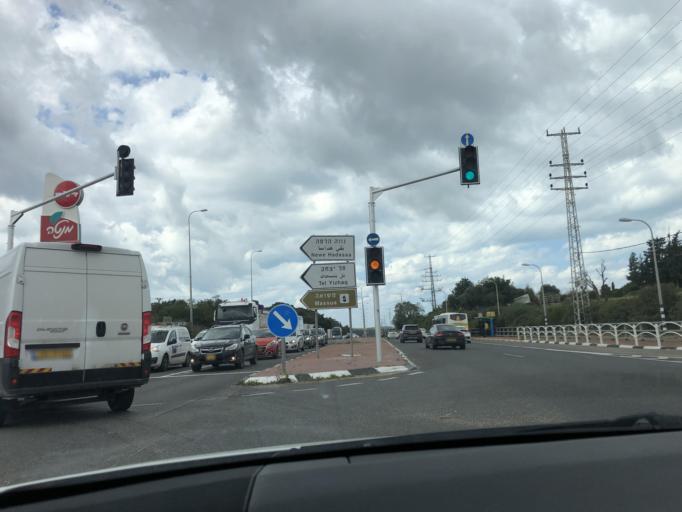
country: IL
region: Central District
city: Even Yehuda
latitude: 32.2556
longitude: 34.8737
